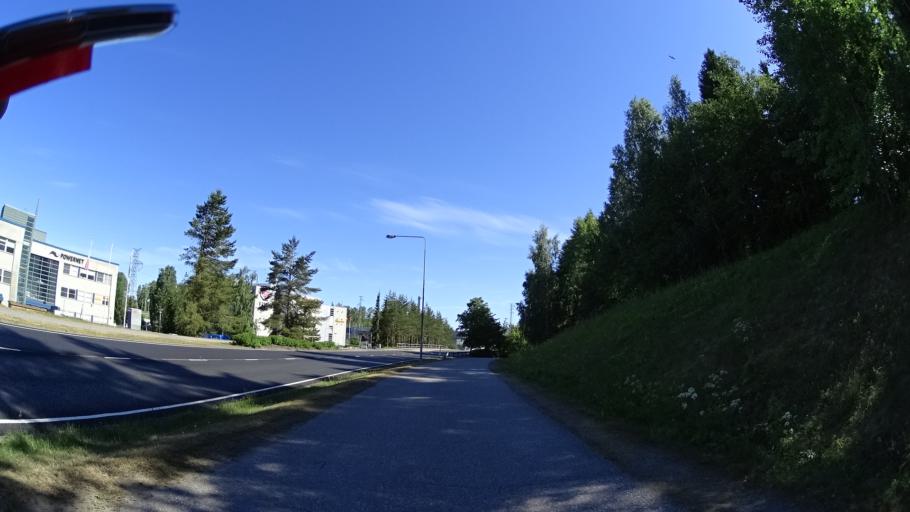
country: FI
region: Uusimaa
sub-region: Helsinki
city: Kilo
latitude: 60.2793
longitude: 24.8244
